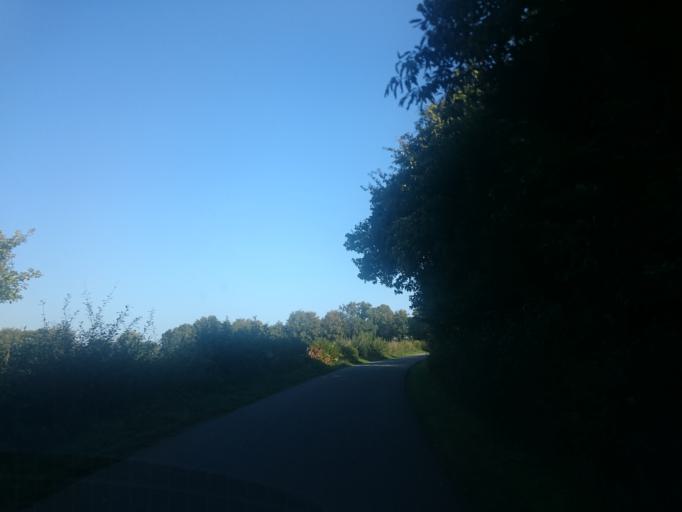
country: FR
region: Brittany
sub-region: Departement d'Ille-et-Vilaine
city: Chanteloup
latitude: 47.9347
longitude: -1.5842
